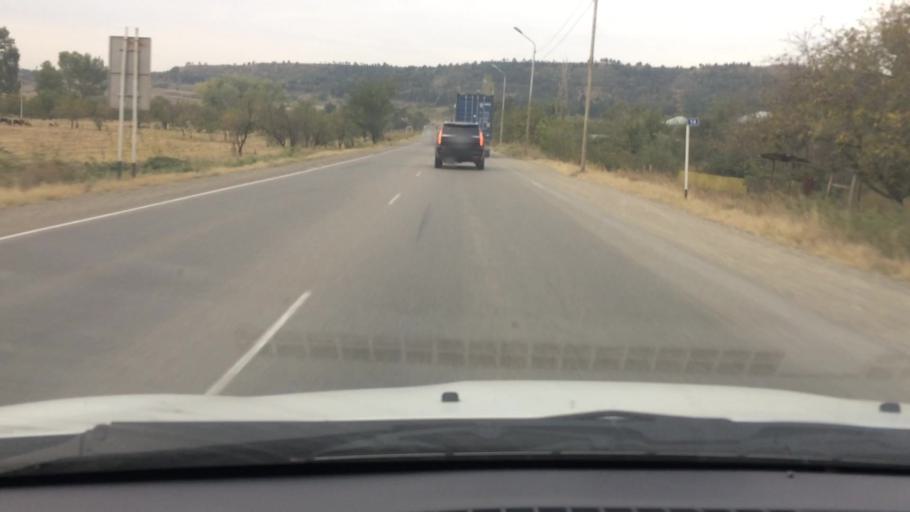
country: GE
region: T'bilisi
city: Tbilisi
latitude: 41.6072
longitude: 44.7835
